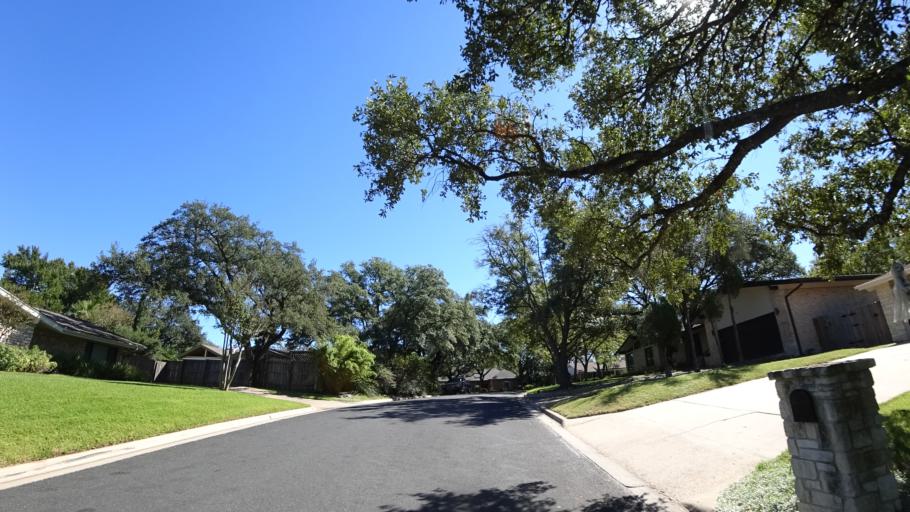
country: US
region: Texas
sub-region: Travis County
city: West Lake Hills
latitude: 30.3383
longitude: -97.7617
